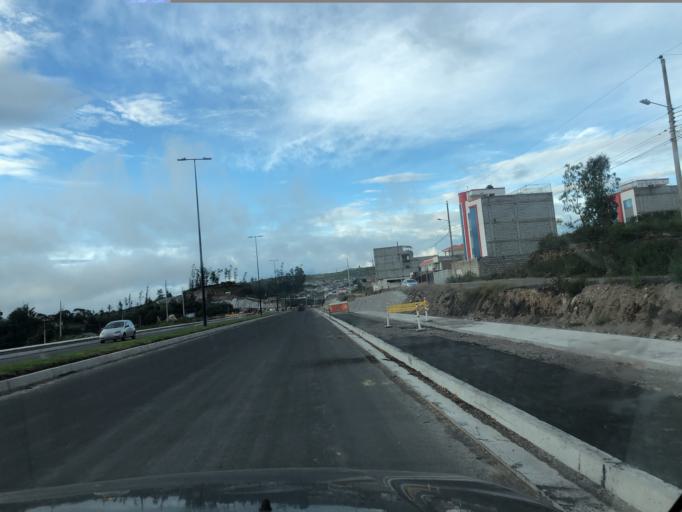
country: EC
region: Imbabura
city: Ibarra
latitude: 0.3532
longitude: -78.1403
